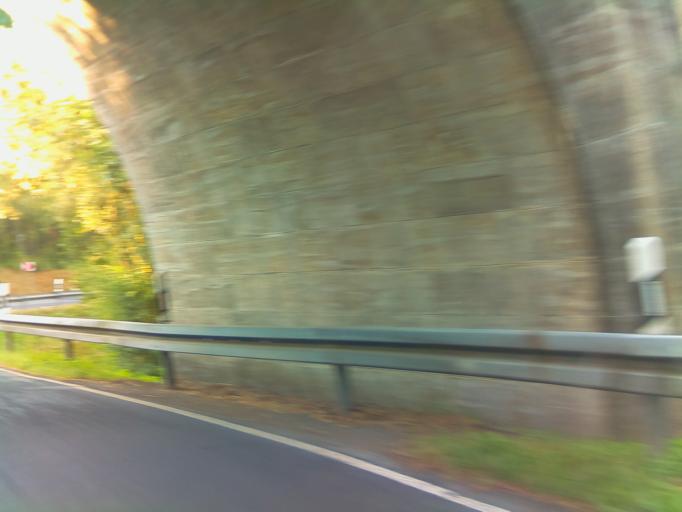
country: DE
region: Bavaria
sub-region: Regierungsbezirk Unterfranken
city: Mellrichstadt
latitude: 50.4457
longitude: 10.3305
